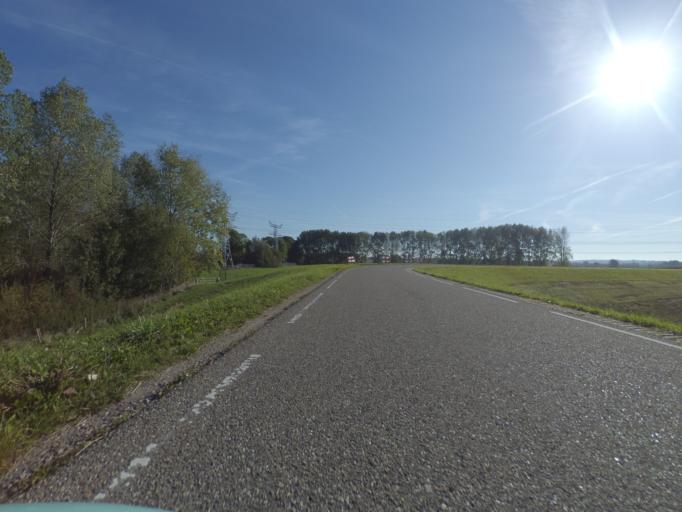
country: NL
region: Gelderland
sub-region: Gemeente Overbetuwe
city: Oosterhout
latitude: 51.8703
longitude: 5.8441
